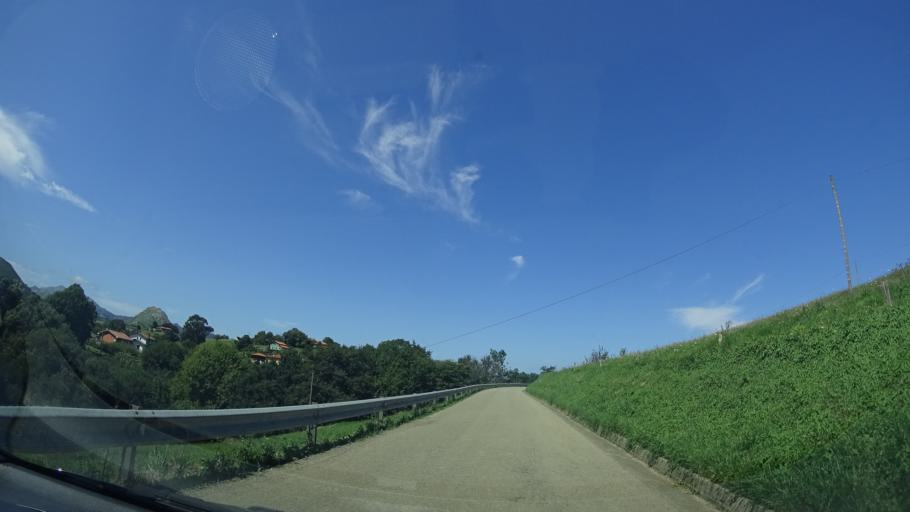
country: ES
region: Asturias
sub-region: Province of Asturias
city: Ribadesella
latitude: 43.4429
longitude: -5.0846
